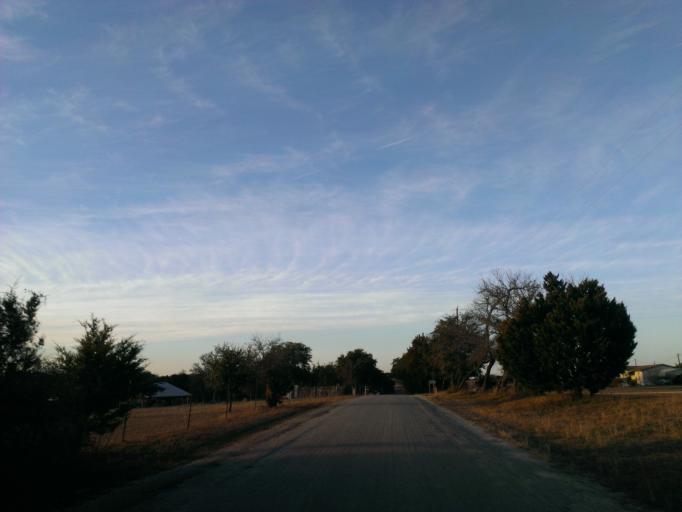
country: US
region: Texas
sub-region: Burnet County
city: Bertram
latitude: 30.7280
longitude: -98.0813
